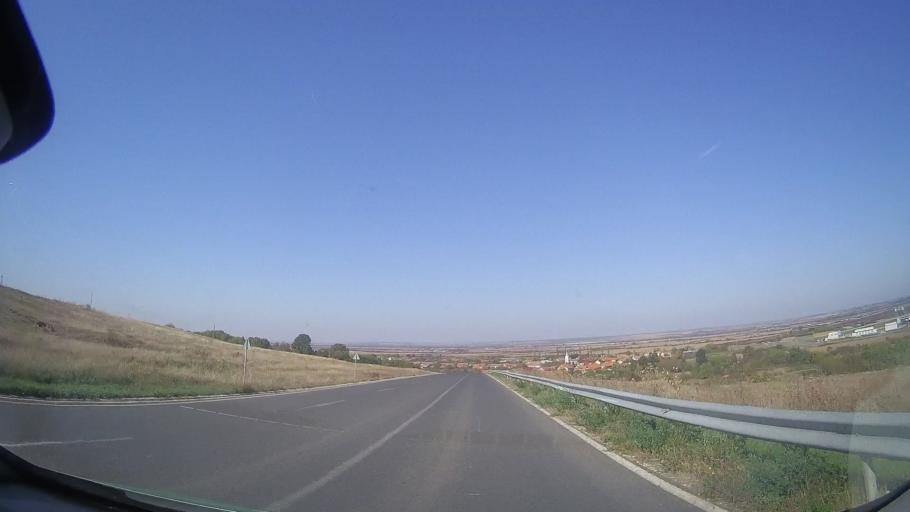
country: RO
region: Timis
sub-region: Comuna Costeiu
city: Costeiu
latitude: 45.7725
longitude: 21.8541
